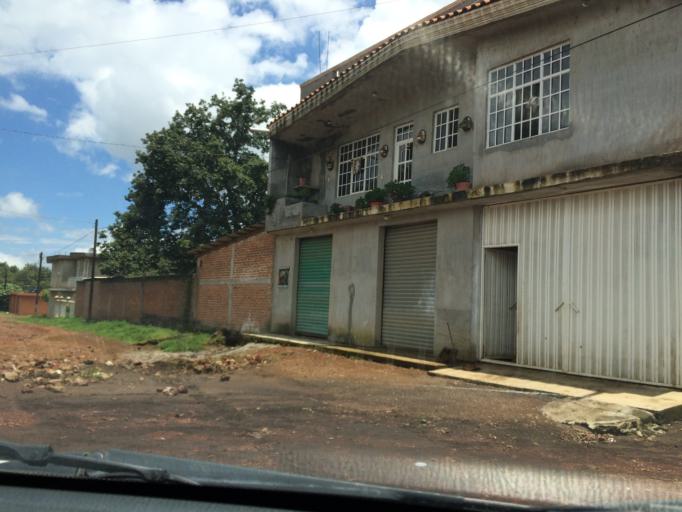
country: MX
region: Michoacan
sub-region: Uruapan
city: Nuevo Zirosto
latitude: 19.5461
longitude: -102.3462
